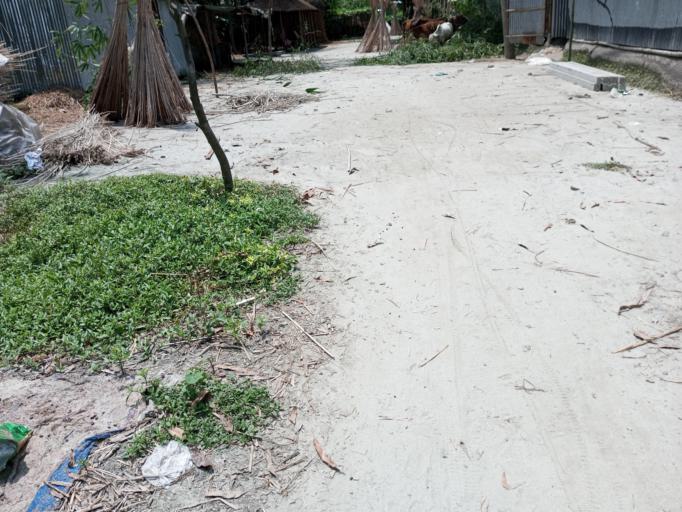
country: BD
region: Rangpur Division
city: Rangpur
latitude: 25.9050
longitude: 89.2711
